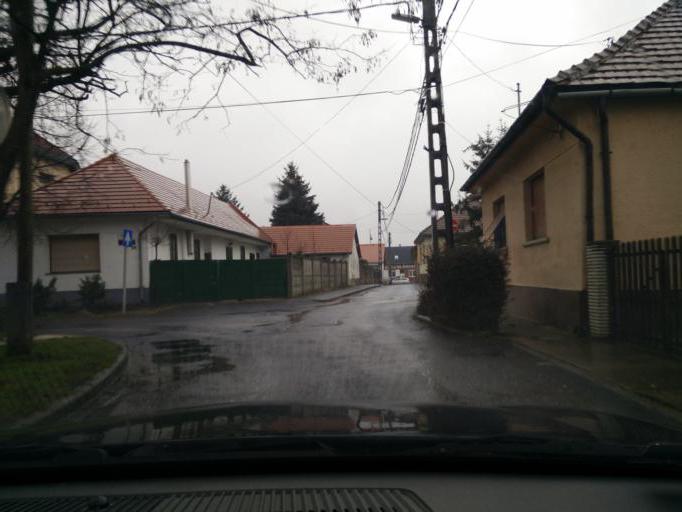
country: HU
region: Pest
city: Pilisvorosvar
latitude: 47.6194
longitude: 18.9088
